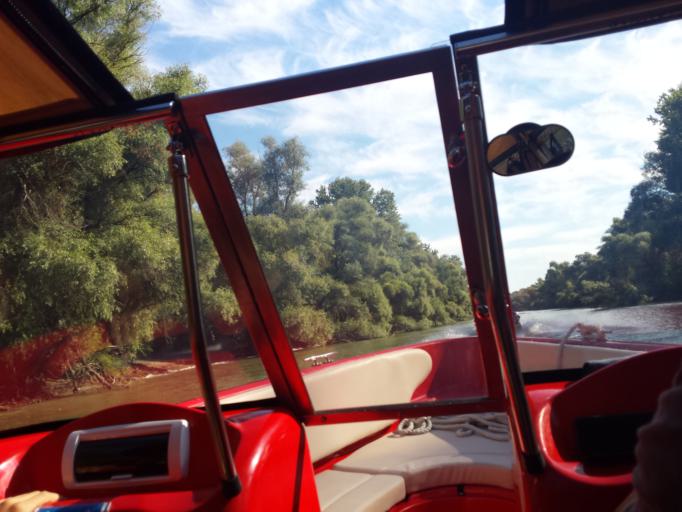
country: RO
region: Tulcea
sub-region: Comuna Nufaru
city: Nufaru
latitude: 45.2179
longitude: 28.8739
